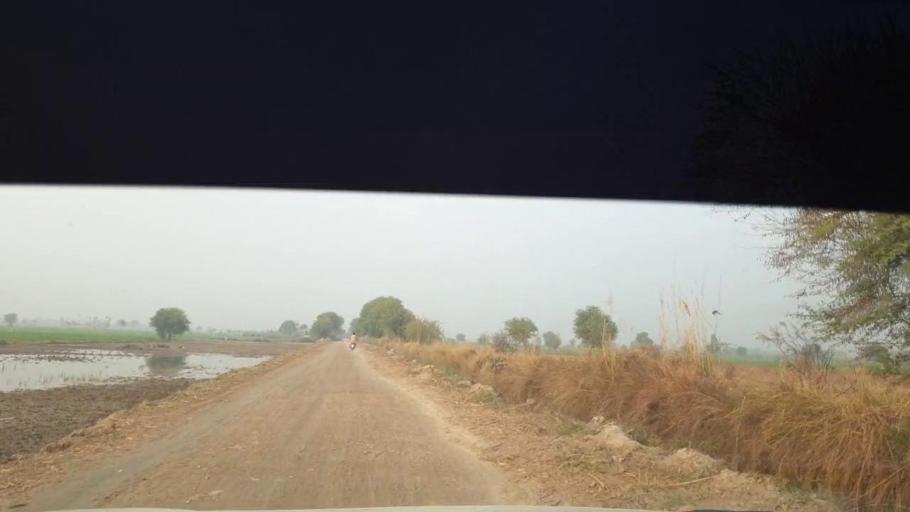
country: PK
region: Sindh
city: Berani
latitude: 25.8383
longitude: 68.8910
